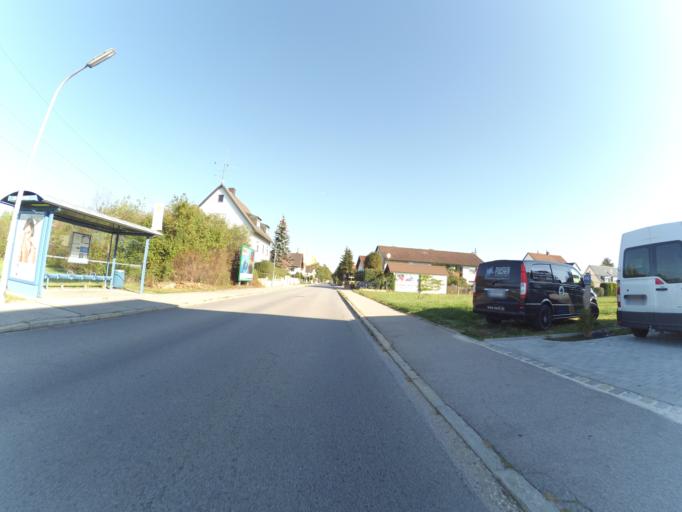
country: DE
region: Bavaria
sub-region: Upper Bavaria
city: Oberschleissheim
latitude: 48.2022
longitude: 11.5535
